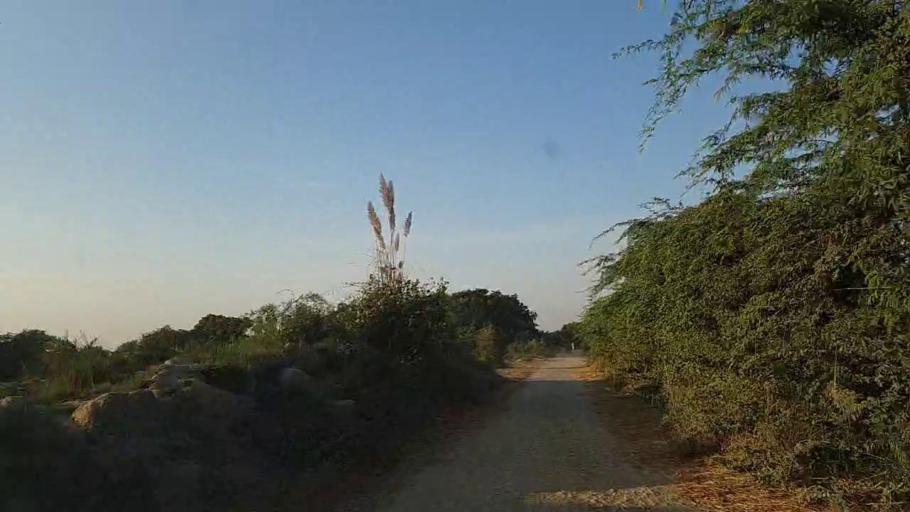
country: PK
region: Sindh
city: Mirpur Batoro
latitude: 24.7103
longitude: 68.2149
